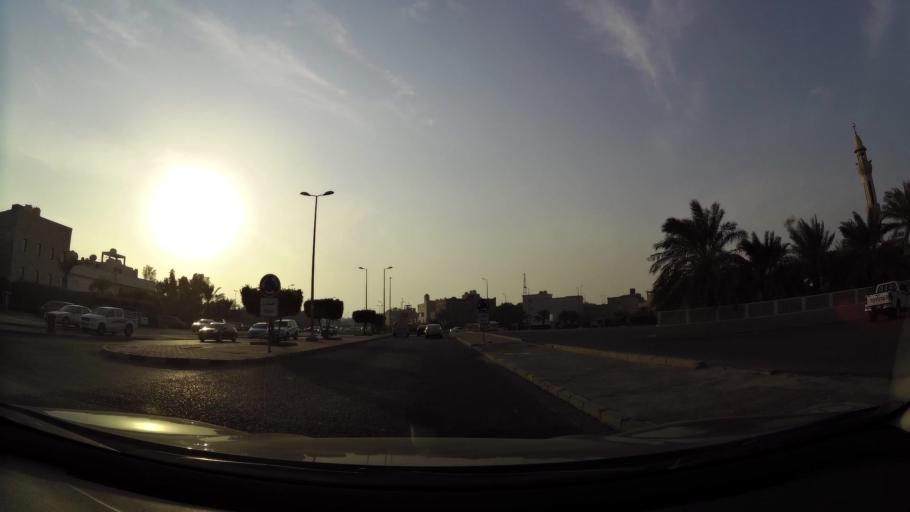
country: KW
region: Mubarak al Kabir
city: Sabah as Salim
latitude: 29.2499
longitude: 48.0721
